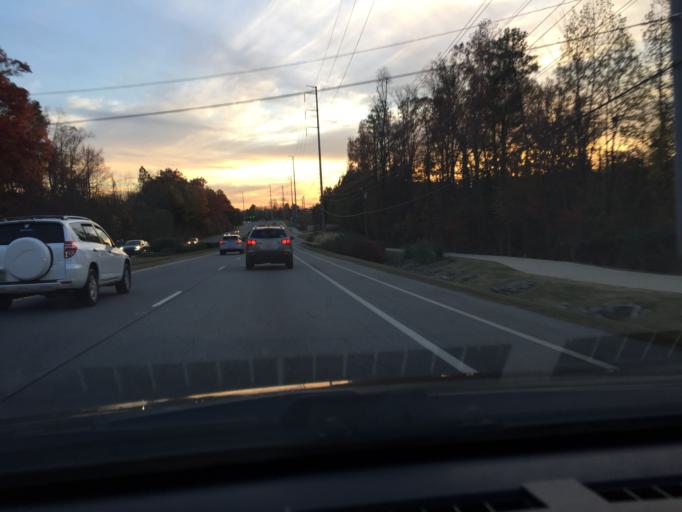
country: US
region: Georgia
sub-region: Fulton County
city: Johns Creek
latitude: 34.0448
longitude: -84.1804
